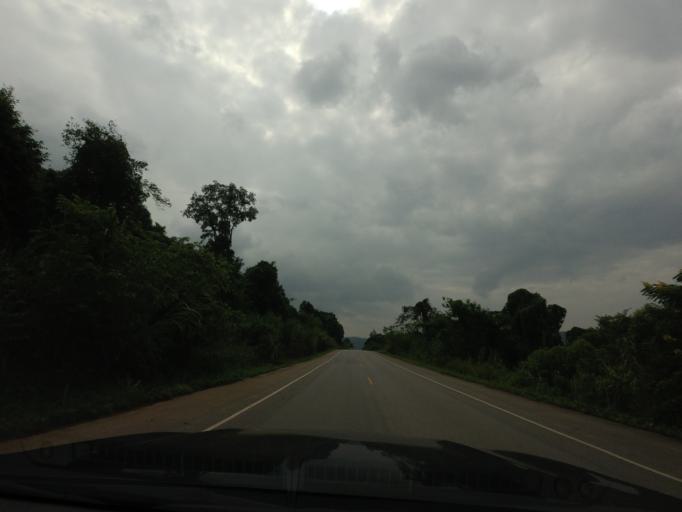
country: TH
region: Loei
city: Dan Sai
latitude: 17.2152
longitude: 101.1725
